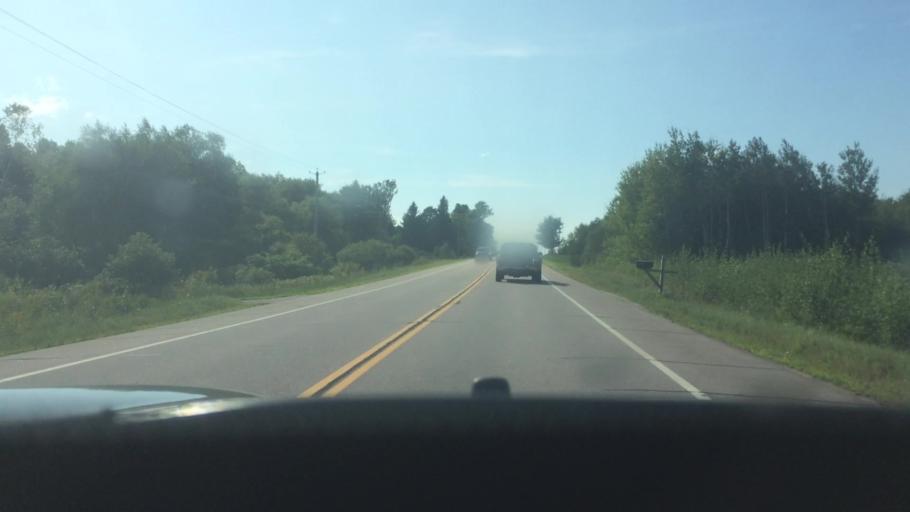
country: US
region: New York
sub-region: Franklin County
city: Malone
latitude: 44.8521
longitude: -74.2100
